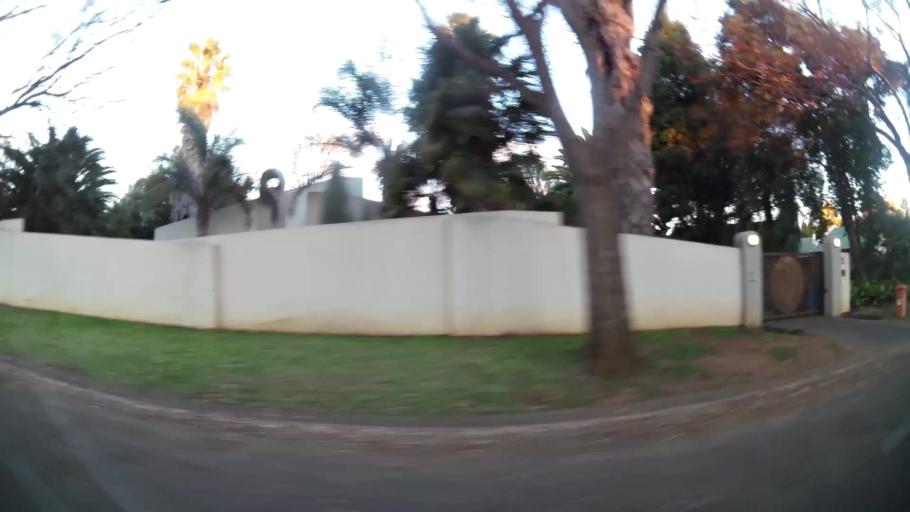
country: ZA
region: North-West
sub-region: Dr Kenneth Kaunda District Municipality
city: Potchefstroom
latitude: -26.7243
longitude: 27.1102
